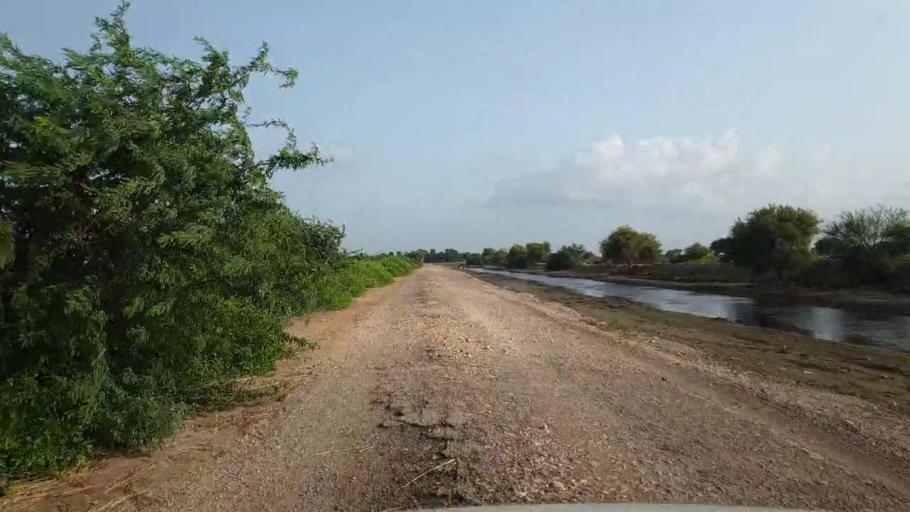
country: PK
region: Sindh
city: Kario
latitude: 24.8418
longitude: 68.6523
